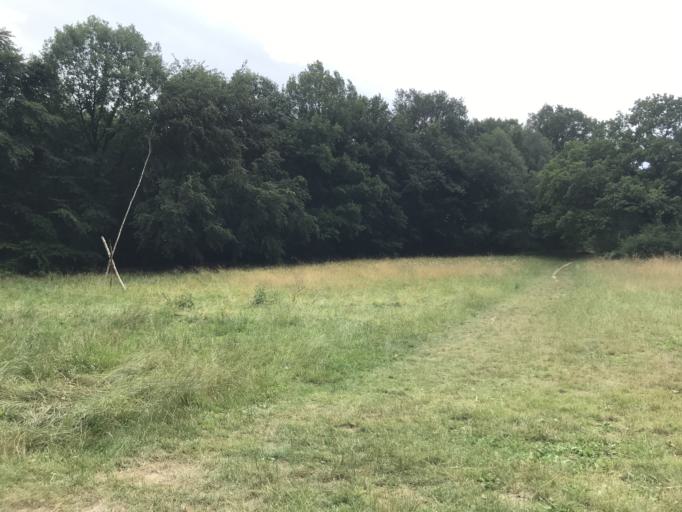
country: DE
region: Rheinland-Pfalz
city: Waldalgesheim
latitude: 49.9709
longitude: 7.8344
